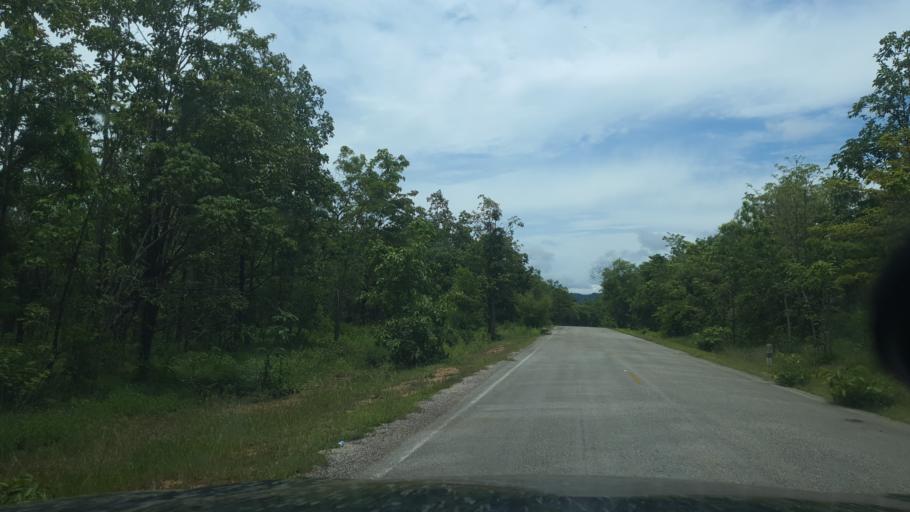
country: TH
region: Lampang
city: Soem Ngam
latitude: 18.0417
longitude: 99.3677
